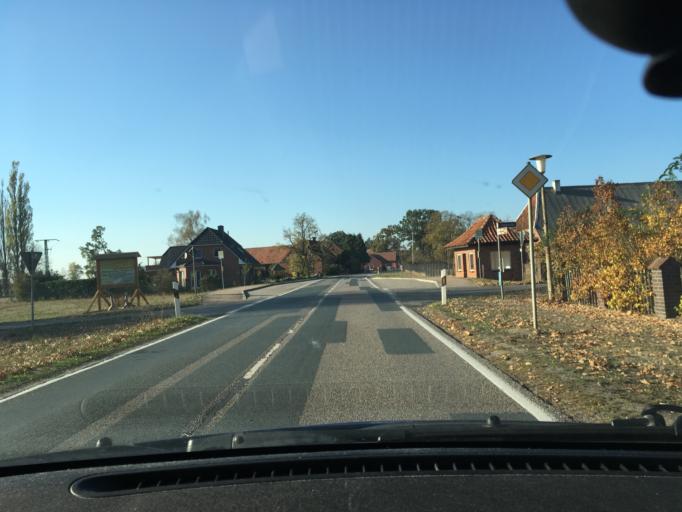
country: DE
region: Lower Saxony
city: Damnatz
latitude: 53.1713
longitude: 11.1676
